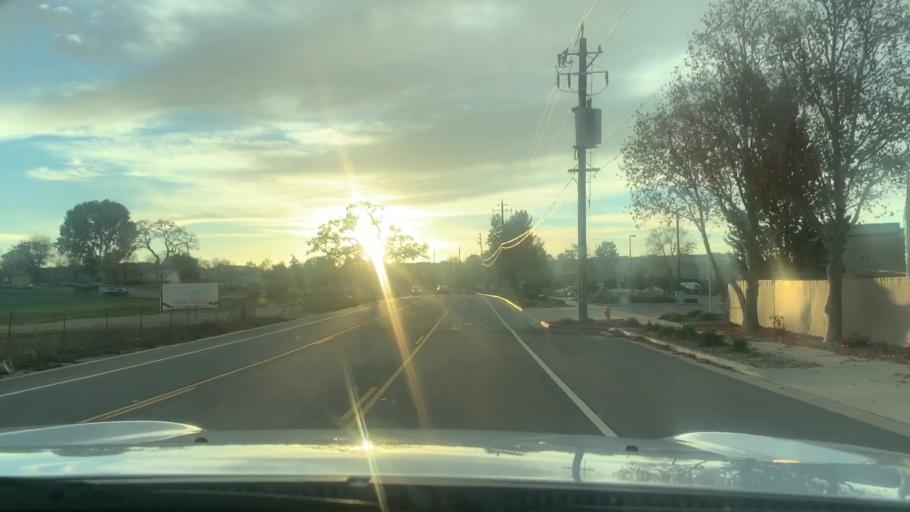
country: US
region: California
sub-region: San Luis Obispo County
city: Paso Robles
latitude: 35.6427
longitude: -120.6541
